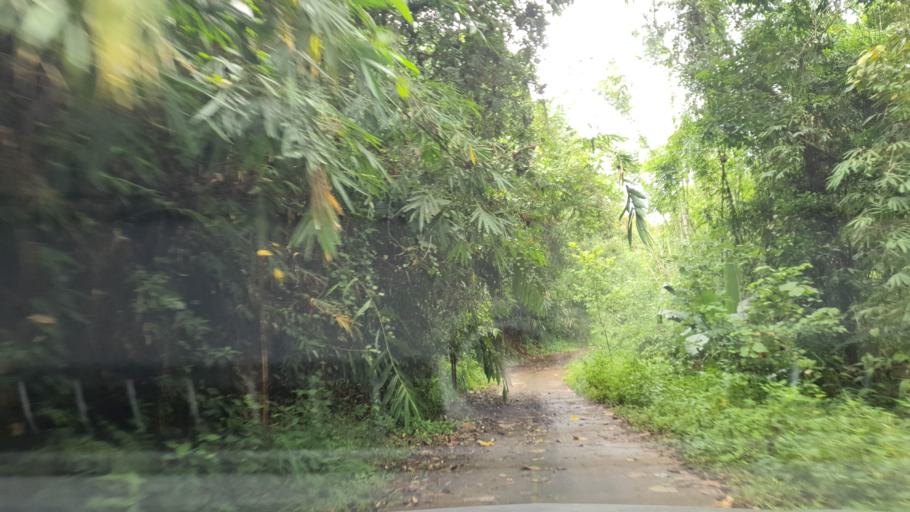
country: TH
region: Chiang Mai
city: Mae On
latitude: 18.9272
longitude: 99.3096
